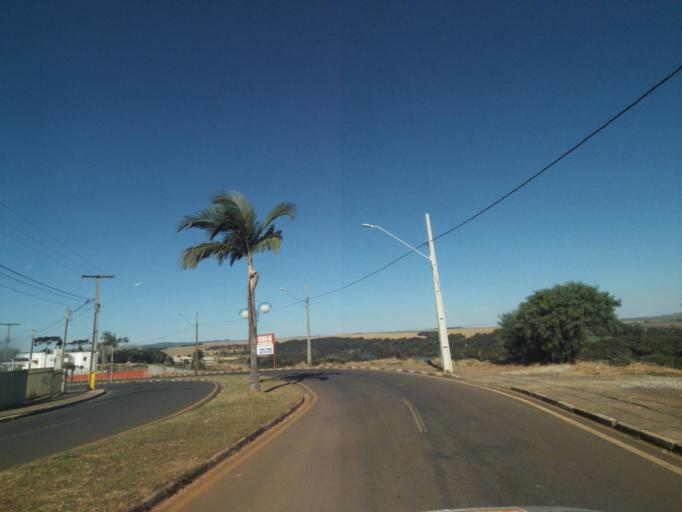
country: BR
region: Parana
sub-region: Tibagi
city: Tibagi
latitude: -24.5243
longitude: -50.4072
